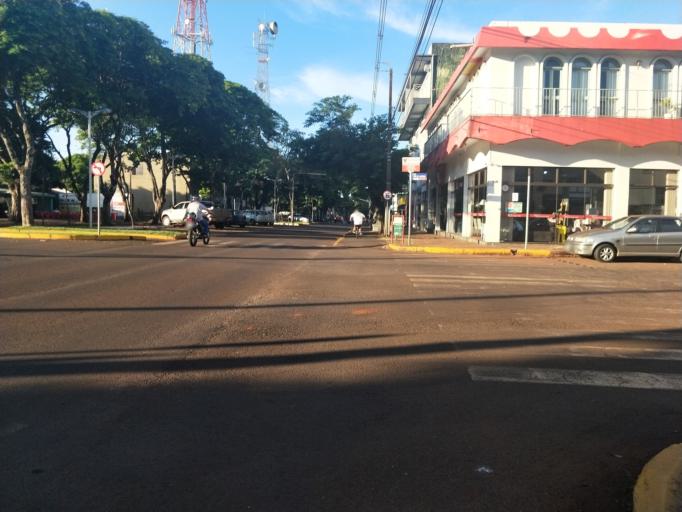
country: BR
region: Parana
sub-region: Marechal Candido Rondon
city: Marechal Candido Rondon
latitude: -24.5601
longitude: -54.0577
